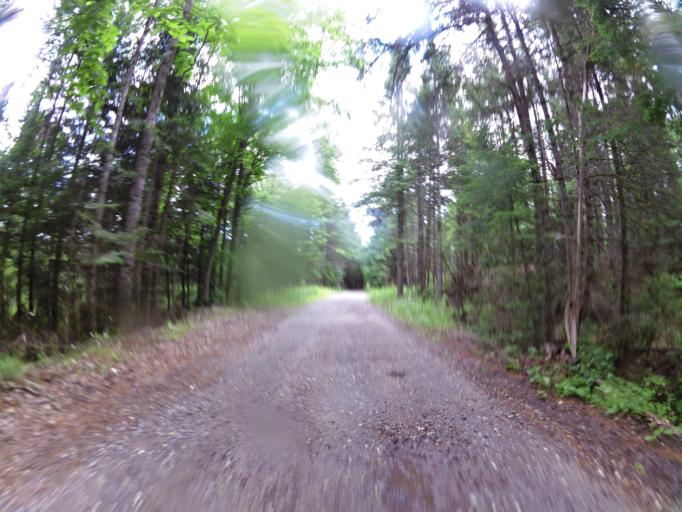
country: CA
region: Ontario
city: Renfrew
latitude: 45.0807
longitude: -76.7205
